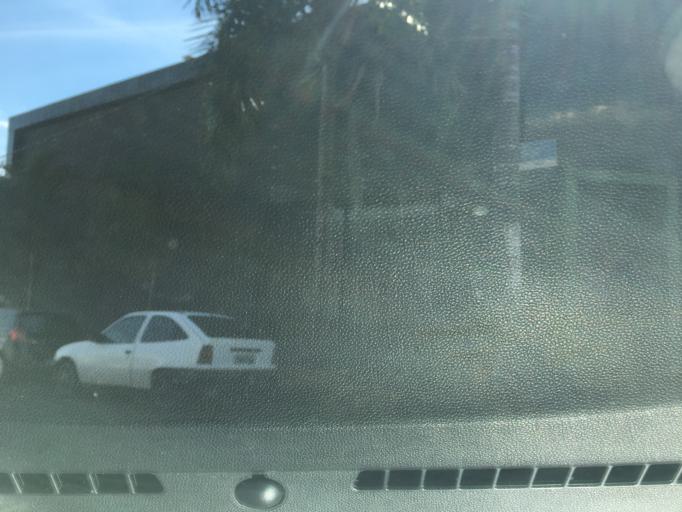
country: BR
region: Minas Gerais
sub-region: Uberlandia
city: Uberlandia
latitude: -18.9133
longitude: -48.2777
